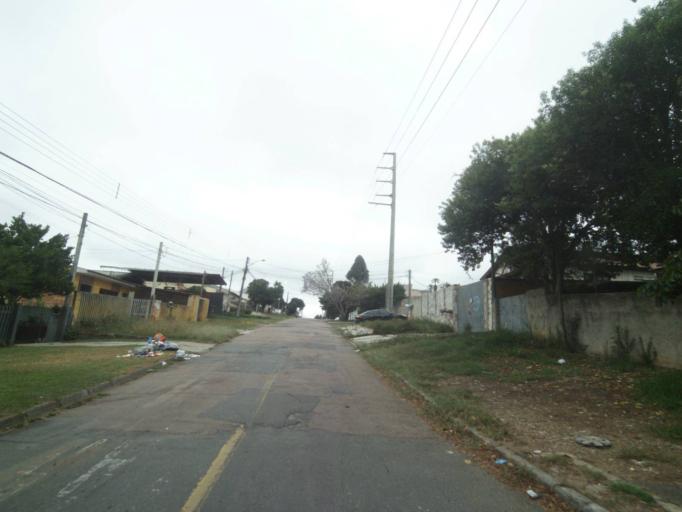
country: BR
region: Parana
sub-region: Sao Jose Dos Pinhais
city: Sao Jose dos Pinhais
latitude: -25.5398
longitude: -49.2847
